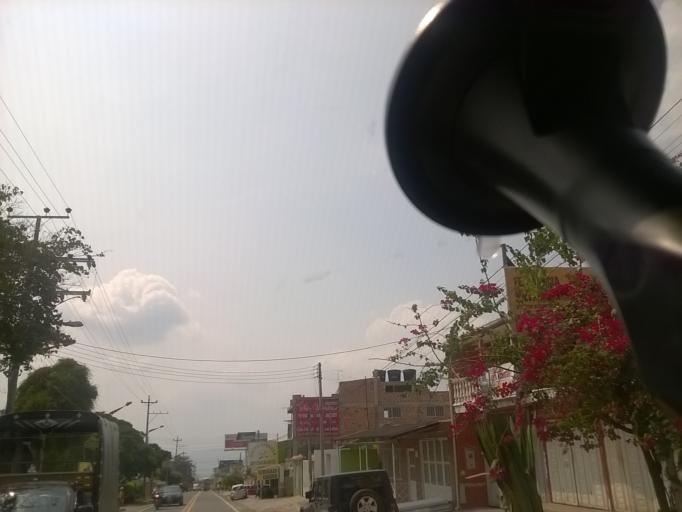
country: CO
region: Cundinamarca
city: San Antonio del Tequendama
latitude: 4.6321
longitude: -74.4535
